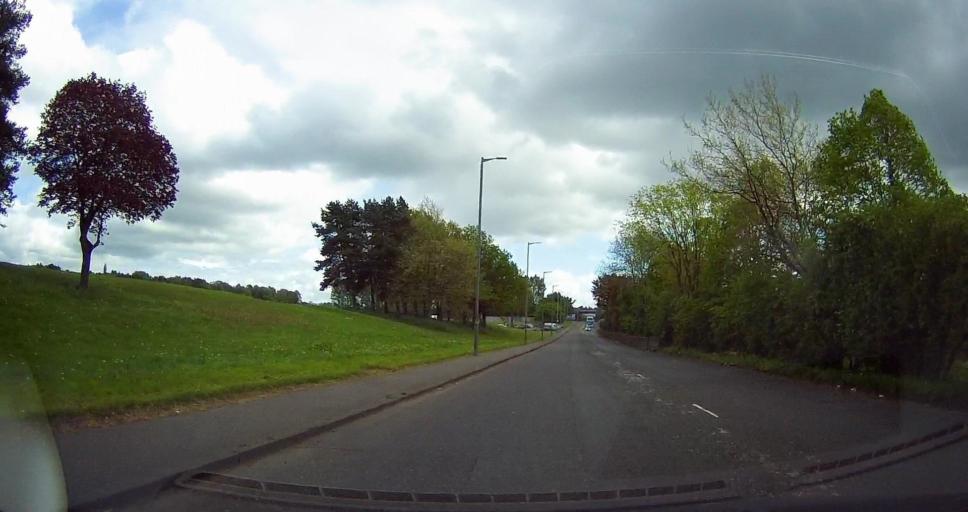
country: GB
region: Scotland
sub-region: Falkirk
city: Larbert
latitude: 56.0097
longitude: -3.8193
